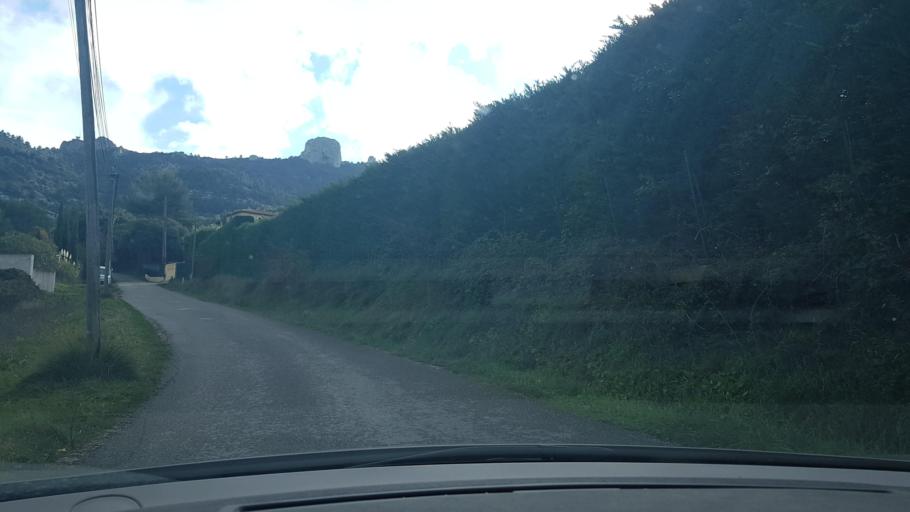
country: FR
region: Provence-Alpes-Cote d'Azur
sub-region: Departement des Bouches-du-Rhone
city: Simiane-Collongue
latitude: 43.4165
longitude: 5.4628
